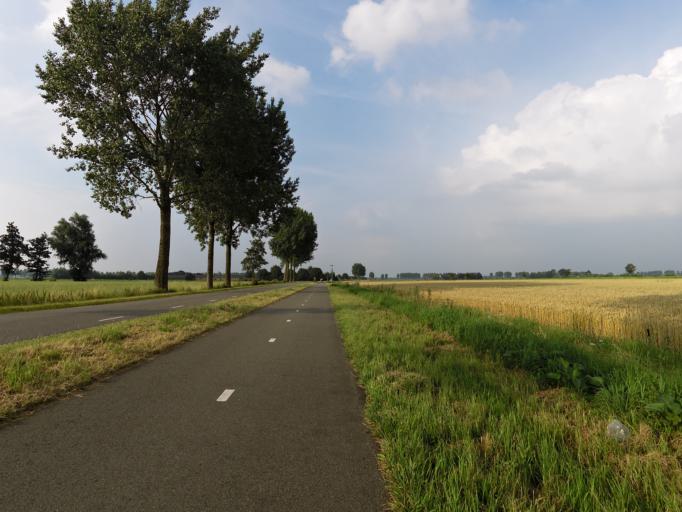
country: NL
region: Gelderland
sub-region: Gemeente Duiven
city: Duiven
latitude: 51.9680
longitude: 6.0355
